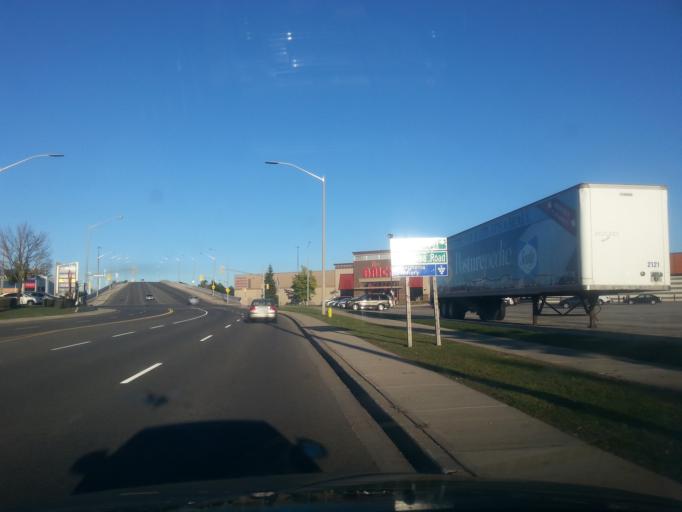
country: CA
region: Ontario
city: Concord
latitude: 43.7937
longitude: -79.5443
